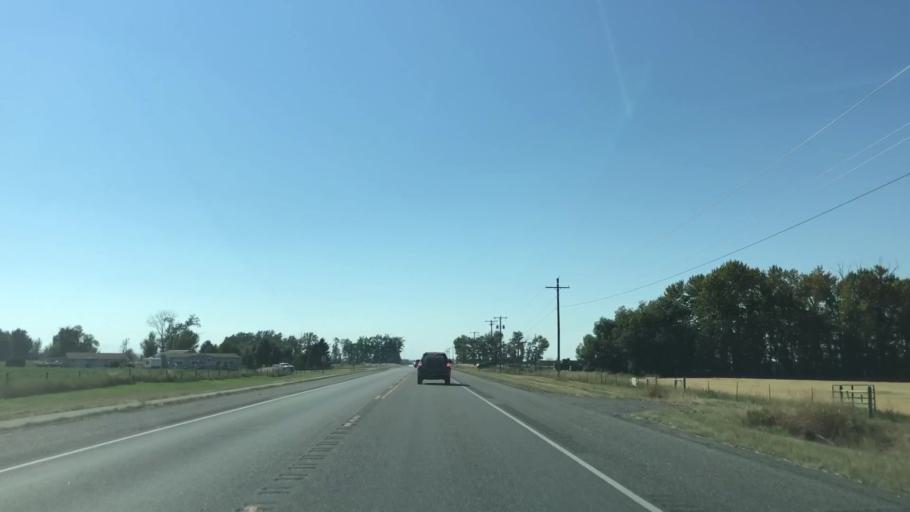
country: US
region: Montana
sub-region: Gallatin County
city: Belgrade
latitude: 45.7292
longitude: -111.1620
